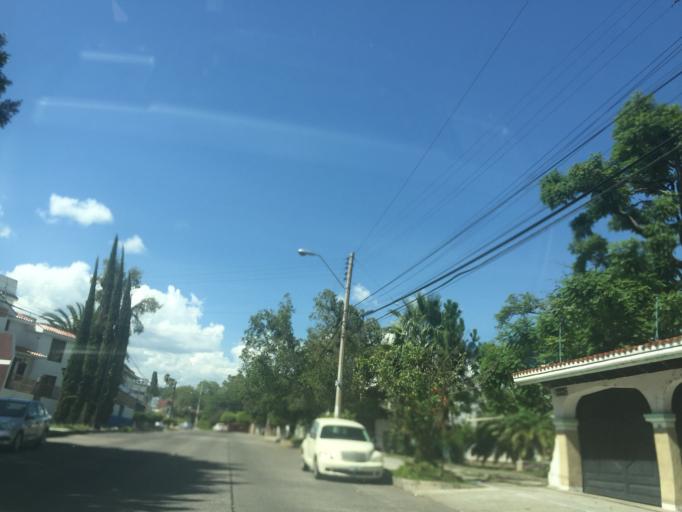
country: MX
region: Guanajuato
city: Leon
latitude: 21.1451
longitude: -101.6928
